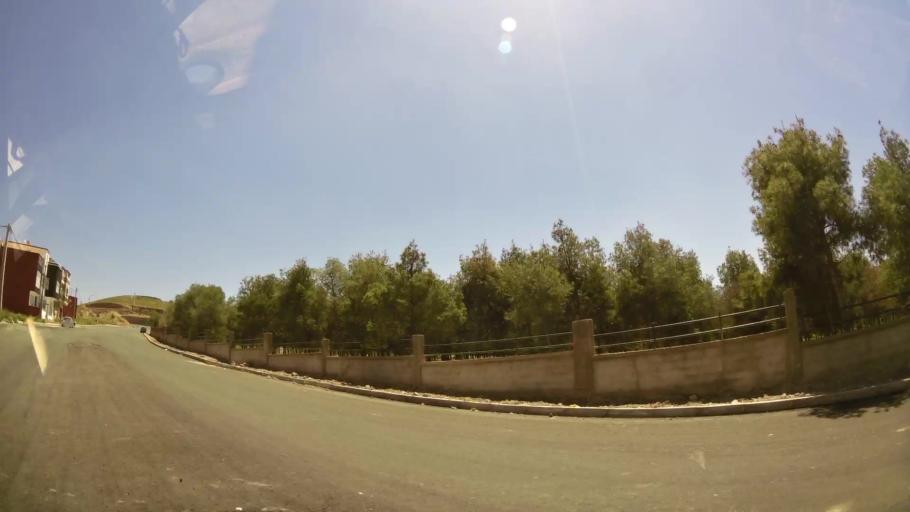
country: MA
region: Oriental
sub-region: Oujda-Angad
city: Oujda
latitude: 34.6533
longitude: -1.9231
